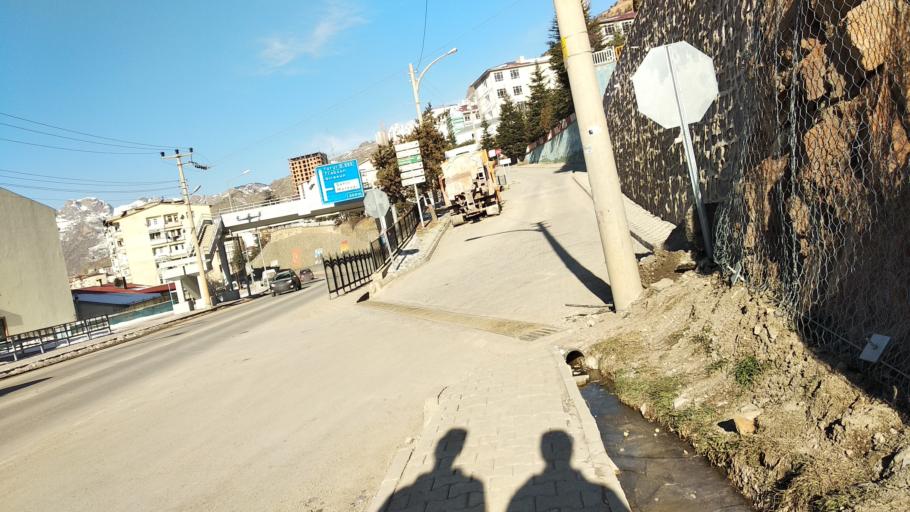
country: TR
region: Gumushane
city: Gumushkhane
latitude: 40.4566
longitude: 39.4897
